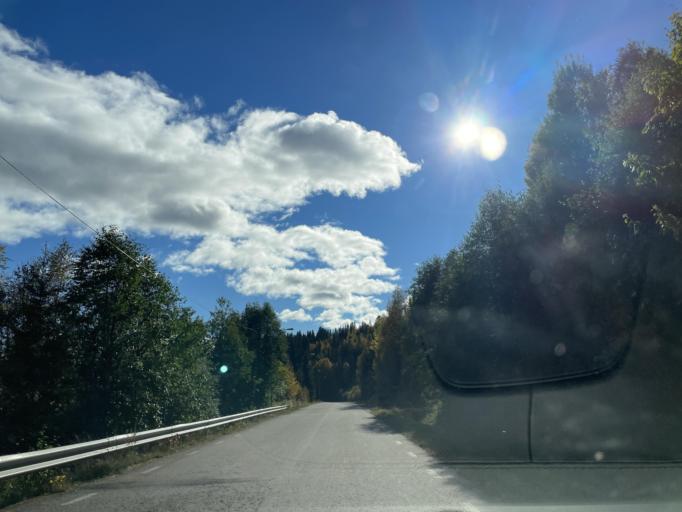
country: SE
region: Dalarna
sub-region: Malung-Saelens kommun
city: Malung
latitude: 61.1566
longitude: 13.2580
